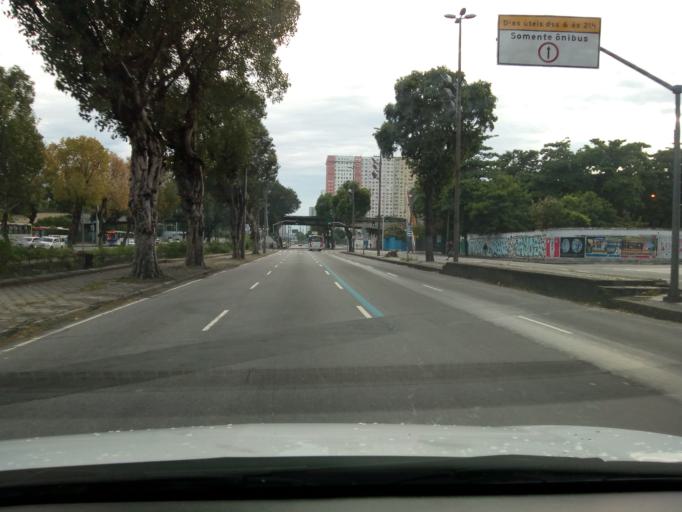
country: BR
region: Rio de Janeiro
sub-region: Rio De Janeiro
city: Rio de Janeiro
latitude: -22.9080
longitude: -43.1992
